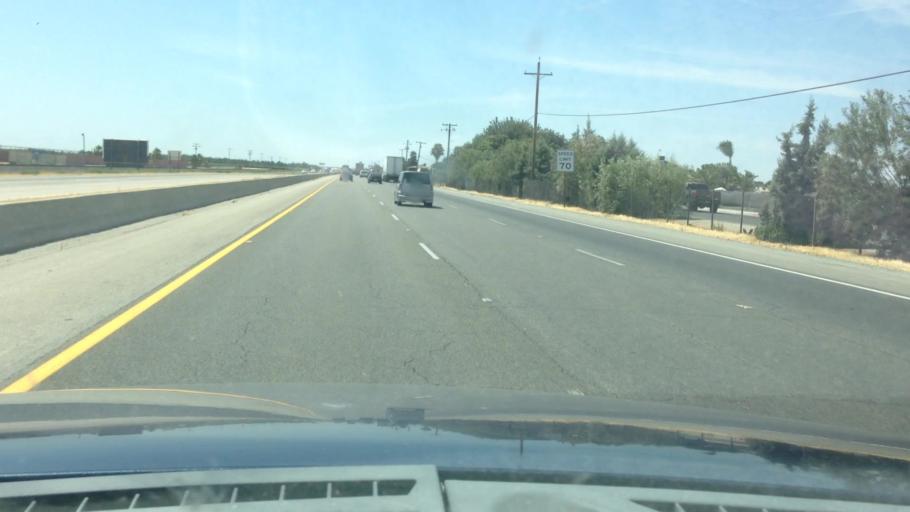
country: US
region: California
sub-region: Kern County
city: McFarland
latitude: 35.6686
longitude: -119.2250
